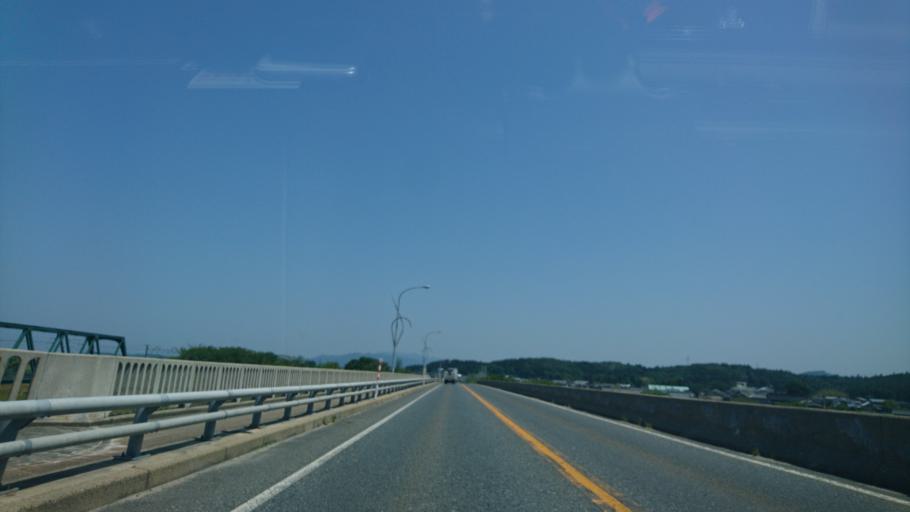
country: JP
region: Niigata
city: Murakami
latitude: 38.1349
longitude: 139.4575
